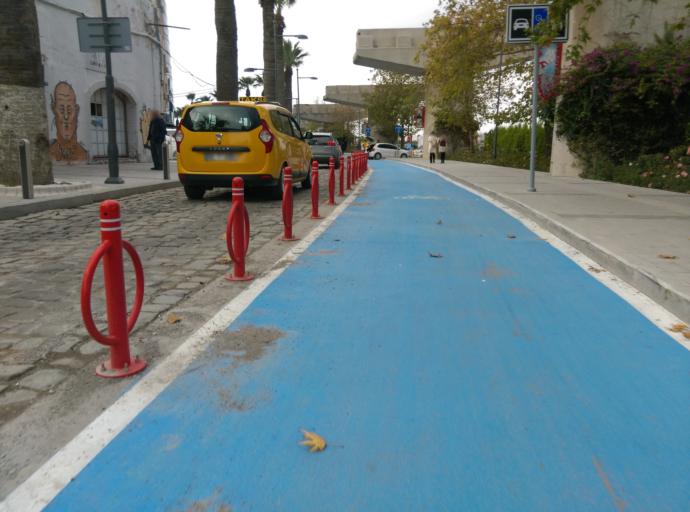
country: TR
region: Izmir
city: Izmir
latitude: 38.4419
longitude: 27.1457
